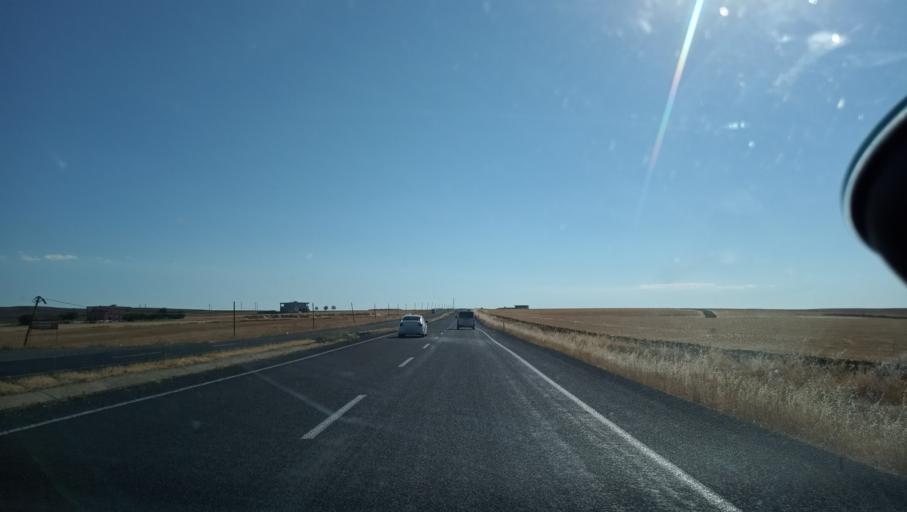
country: TR
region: Diyarbakir
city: Ambar
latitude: 38.0005
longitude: 40.4178
